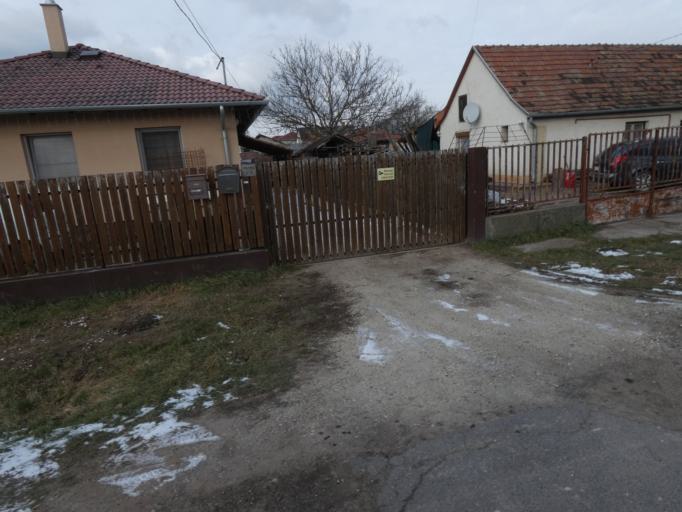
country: HU
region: Pest
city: Szigethalom
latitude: 47.3144
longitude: 18.9868
